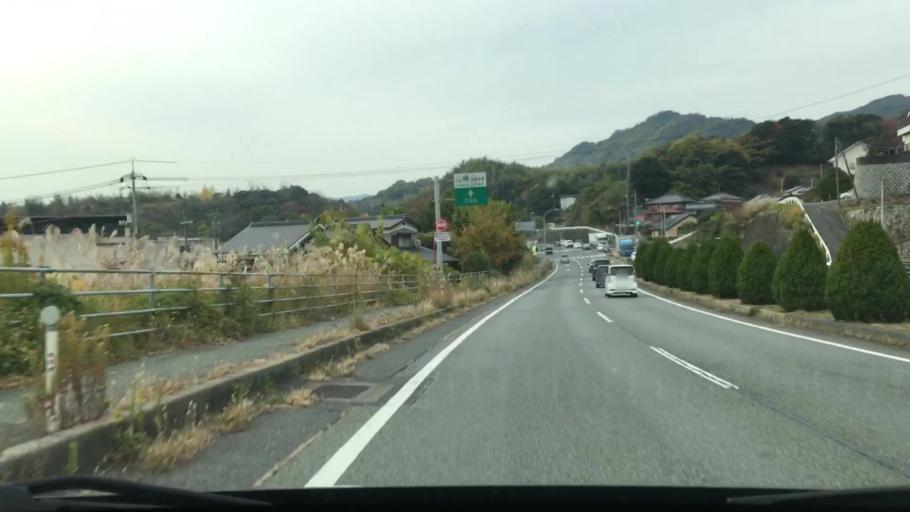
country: JP
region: Yamaguchi
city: Tokuyama
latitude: 34.0753
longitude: 131.7390
